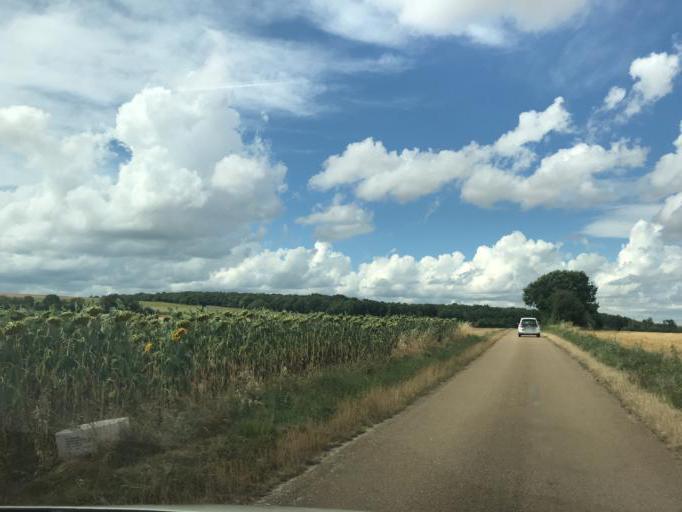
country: FR
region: Bourgogne
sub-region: Departement de l'Yonne
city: Fontenailles
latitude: 47.5838
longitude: 3.3454
